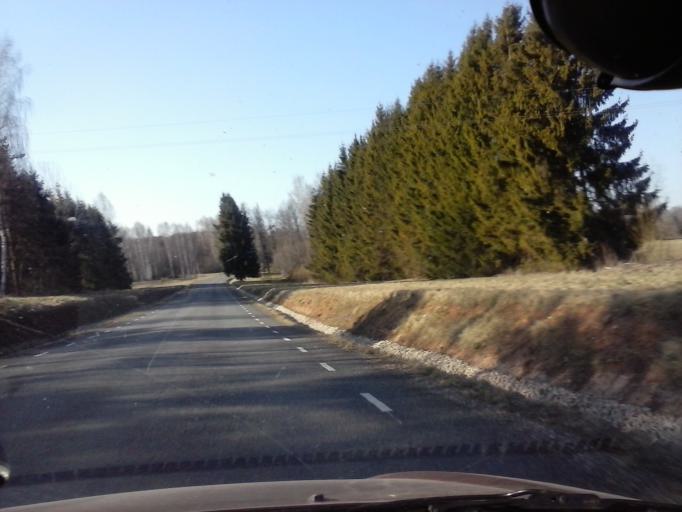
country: EE
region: Tartu
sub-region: UElenurme vald
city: Ulenurme
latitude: 58.1716
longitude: 26.8348
